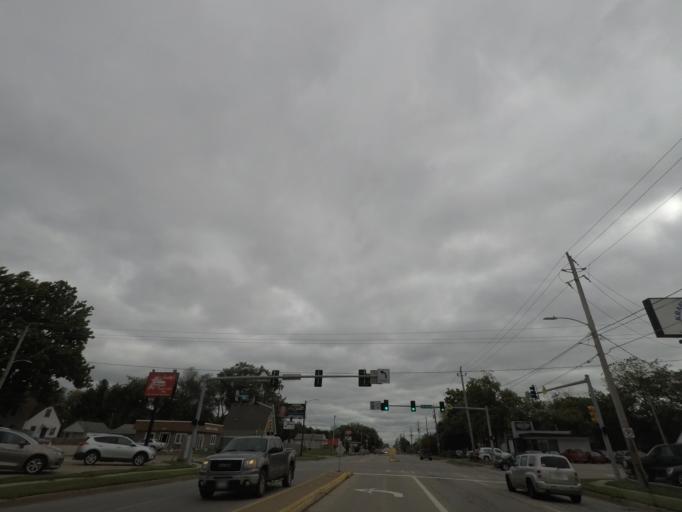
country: US
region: Iowa
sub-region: Warren County
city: Norwalk
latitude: 41.5265
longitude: -93.6358
